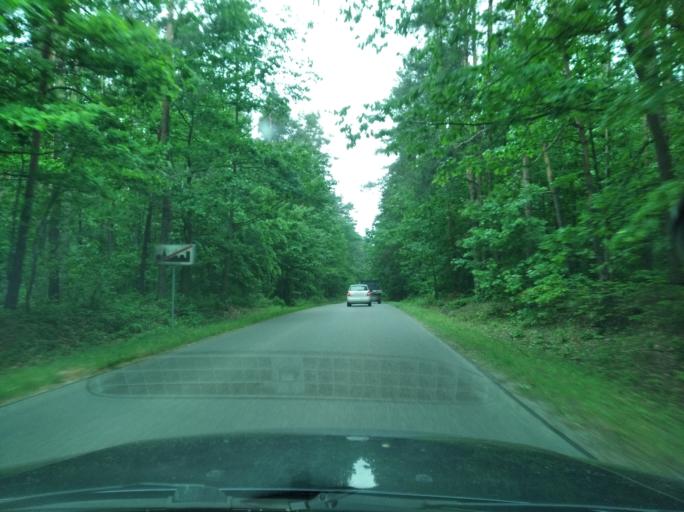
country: PL
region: Subcarpathian Voivodeship
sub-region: Powiat kolbuszowski
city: Niwiska
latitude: 50.1752
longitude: 21.6640
